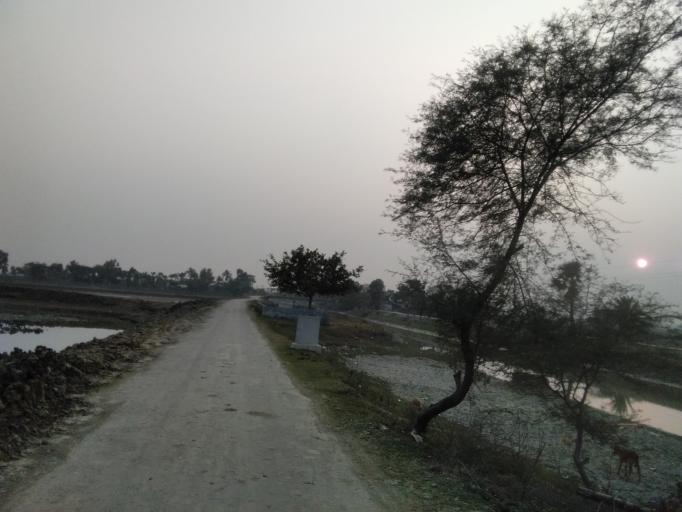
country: BD
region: Khulna
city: Satkhira
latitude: 22.6500
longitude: 89.0140
